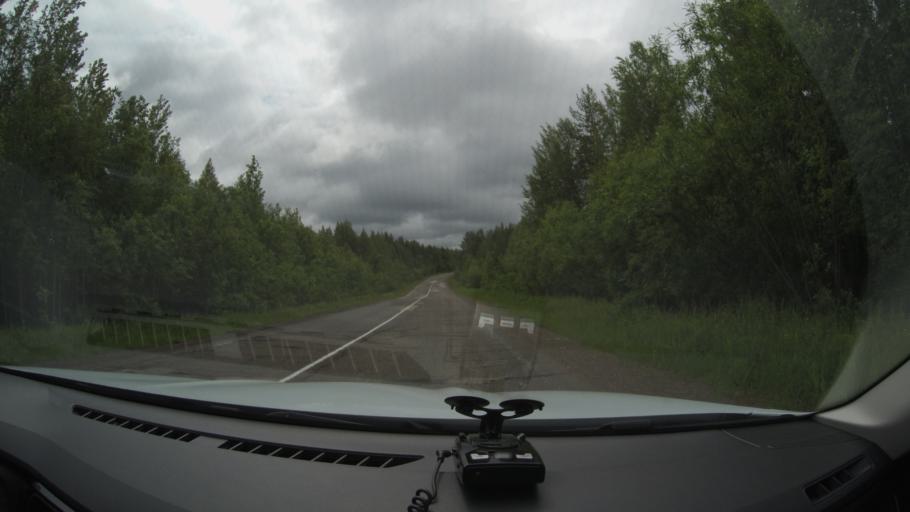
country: RU
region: Komi Republic
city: Nizhniy Odes
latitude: 63.6396
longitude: 54.6461
